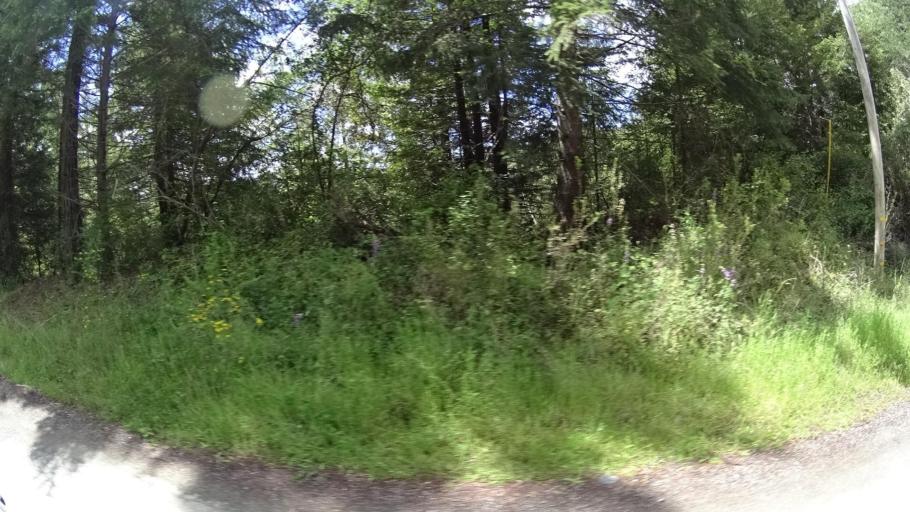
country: US
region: California
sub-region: Humboldt County
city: Blue Lake
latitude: 40.8417
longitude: -123.8954
